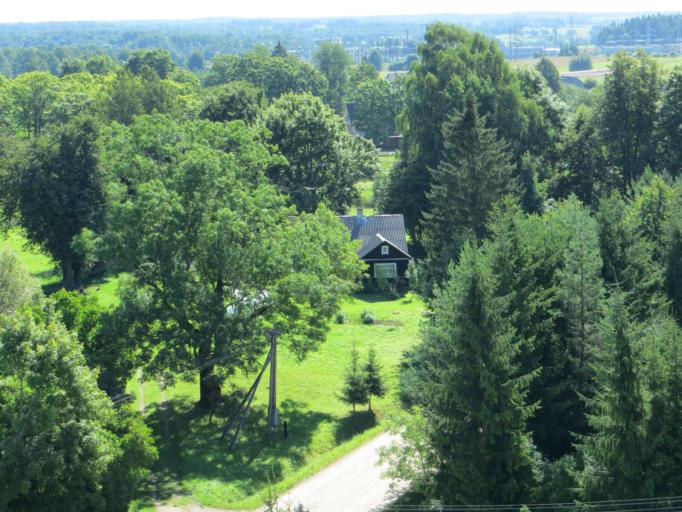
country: LT
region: Utenos apskritis
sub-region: Utena
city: Utena
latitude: 55.5480
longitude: 25.6140
